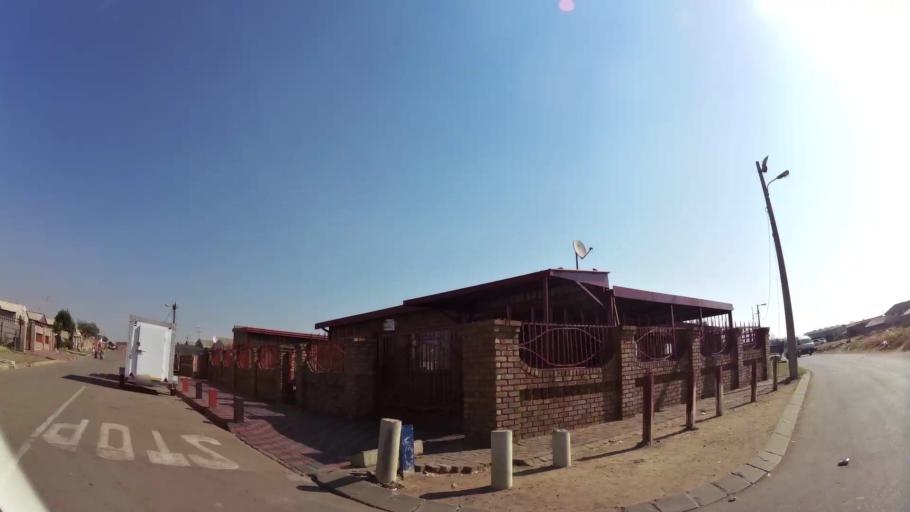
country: ZA
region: Gauteng
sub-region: Ekurhuleni Metropolitan Municipality
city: Benoni
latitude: -26.2172
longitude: 28.2973
